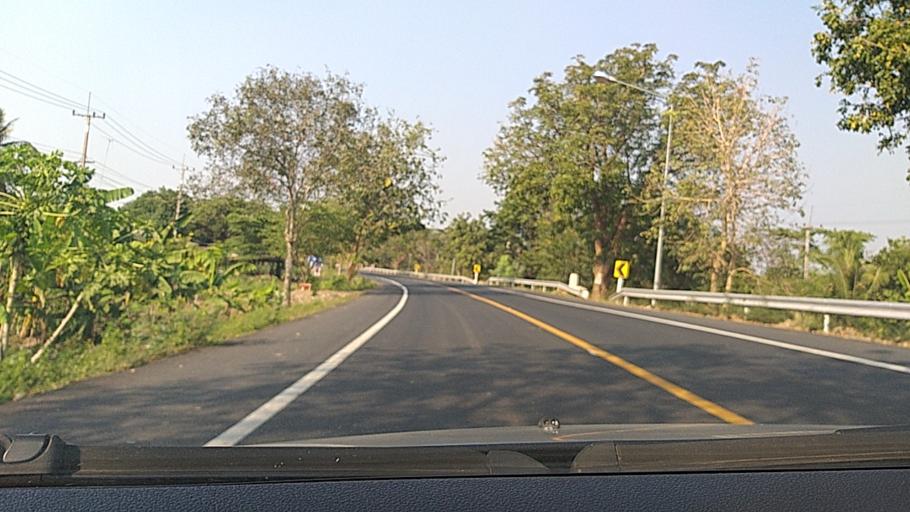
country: TH
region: Sing Buri
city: Phrom Buri
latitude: 14.7644
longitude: 100.4402
